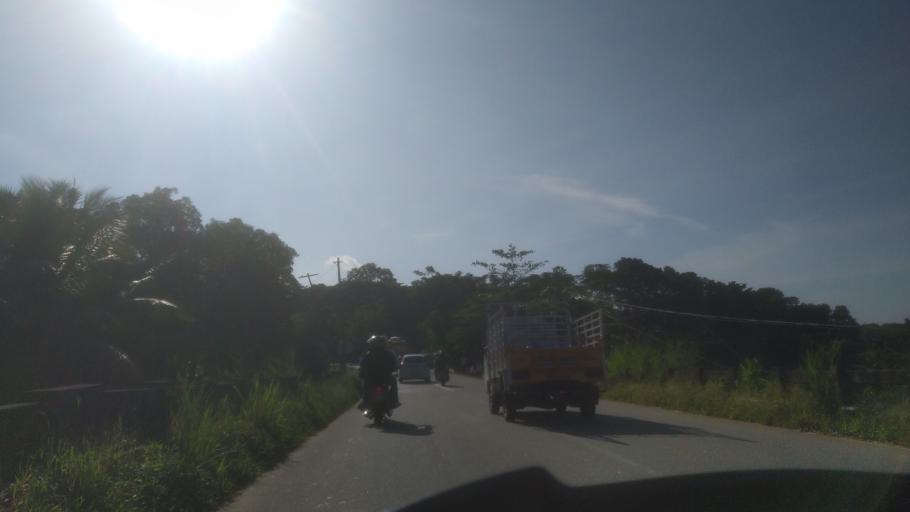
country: IN
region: Kerala
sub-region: Ernakulam
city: Ramamangalam
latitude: 9.9766
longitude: 76.5068
